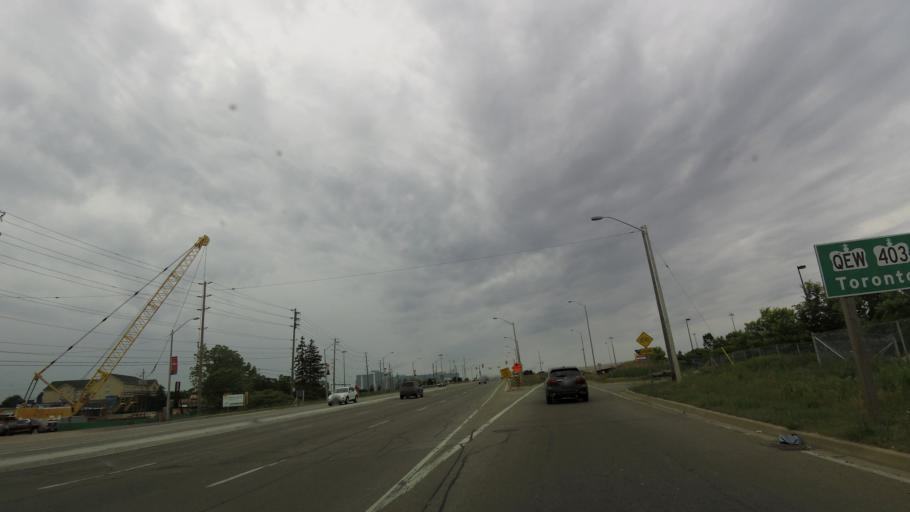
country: CA
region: Ontario
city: Burlington
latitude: 43.3928
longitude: -79.7529
